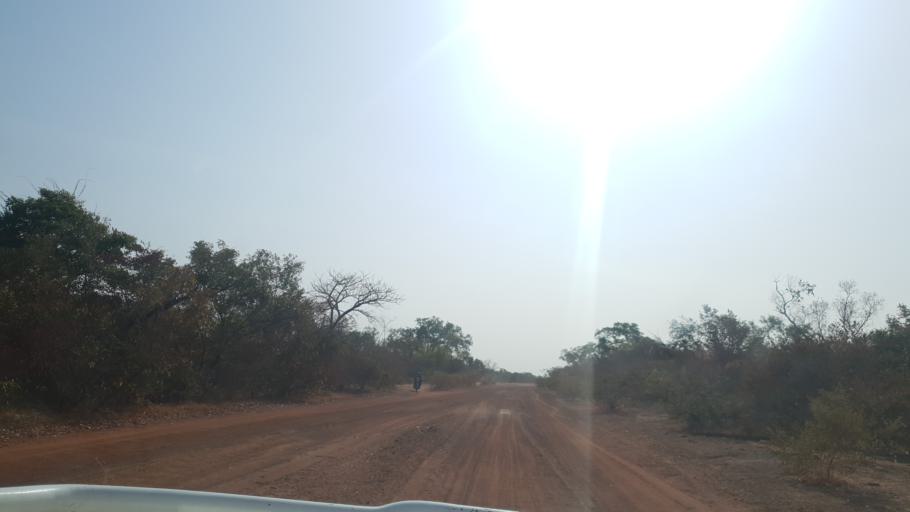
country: ML
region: Koulikoro
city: Dioila
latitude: 12.6939
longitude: -6.7530
